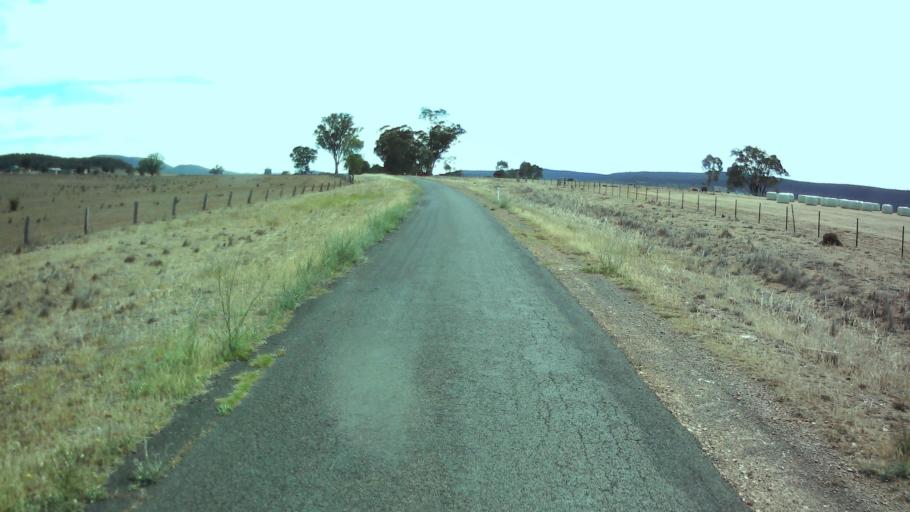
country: AU
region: New South Wales
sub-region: Weddin
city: Grenfell
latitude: -33.8329
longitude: 148.2736
